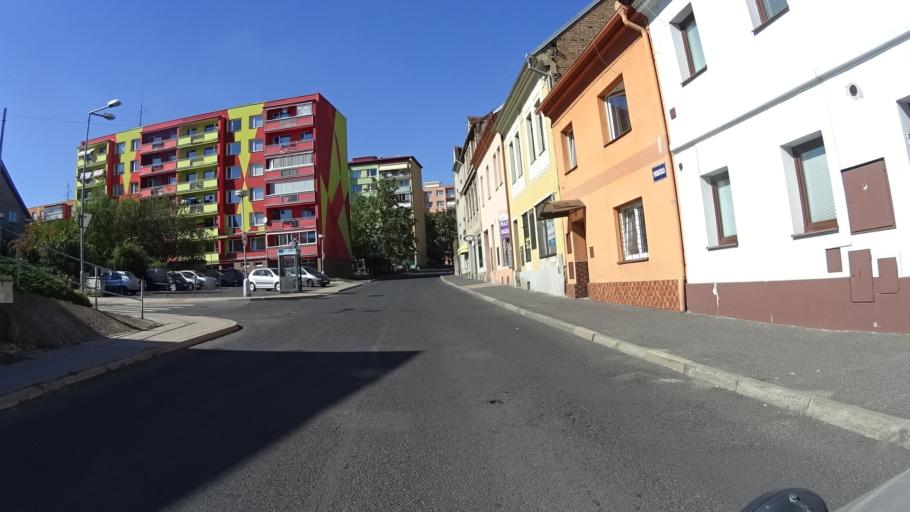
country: CZ
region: Ustecky
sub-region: Okres Litomerice
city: Litomerice
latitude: 50.5453
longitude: 14.1244
